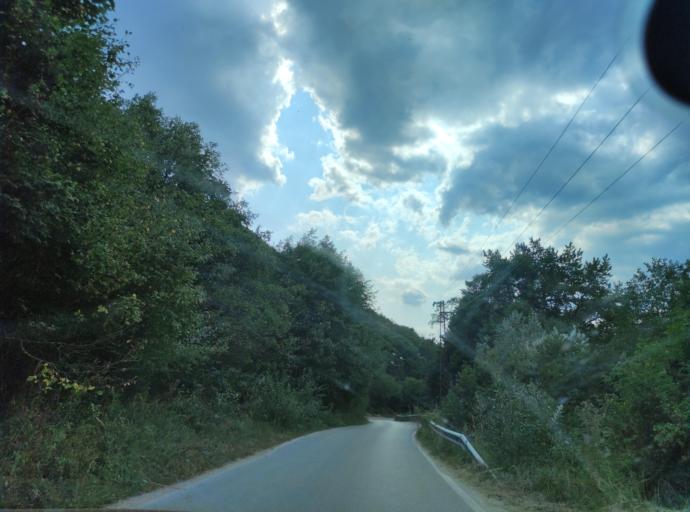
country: BG
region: Blagoevgrad
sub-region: Obshtina Belitsa
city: Belitsa
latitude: 42.0085
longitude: 23.5632
